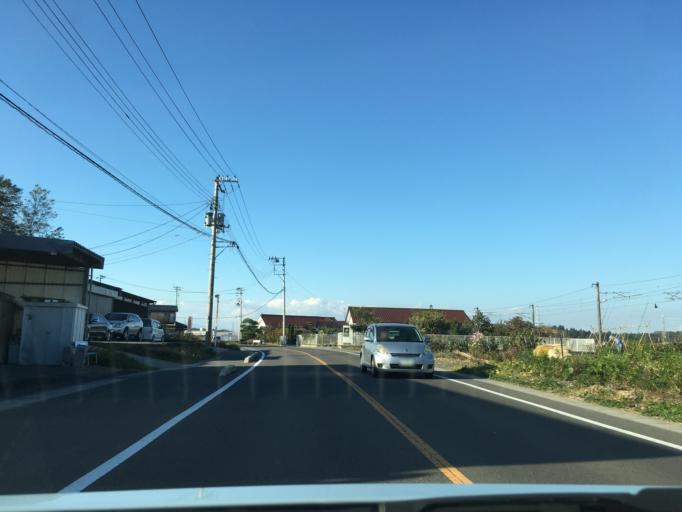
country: JP
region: Fukushima
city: Sukagawa
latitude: 37.3198
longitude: 140.3784
